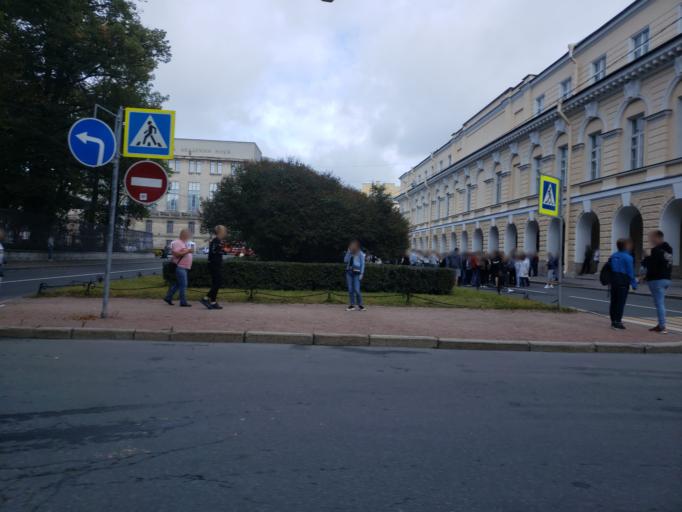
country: RU
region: St.-Petersburg
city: Saint Petersburg
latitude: 59.9430
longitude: 30.2989
